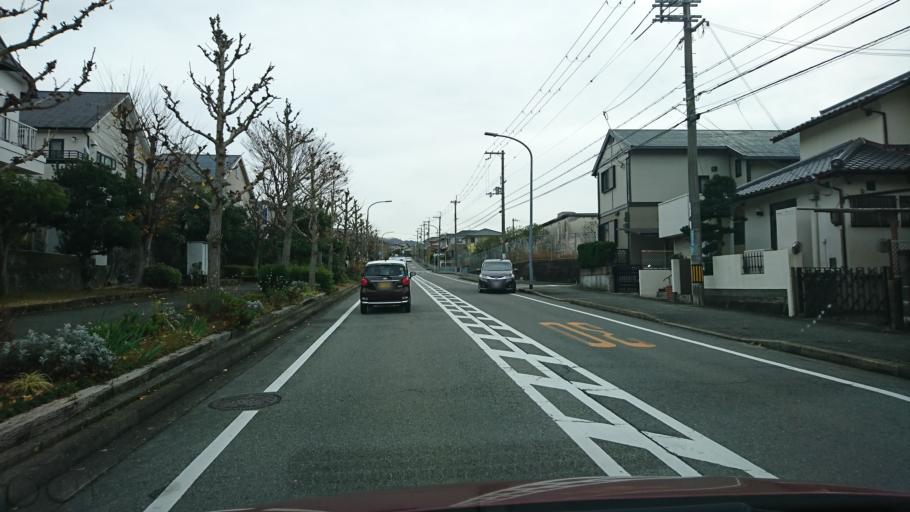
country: JP
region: Osaka
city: Mino
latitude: 34.9004
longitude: 135.4460
